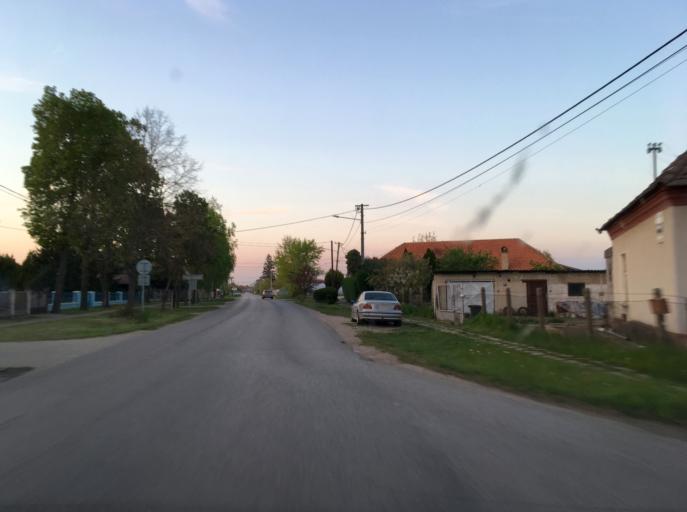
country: SK
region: Nitriansky
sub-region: Okres Nove Zamky
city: Nove Zamky
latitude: 47.9279
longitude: 18.1214
